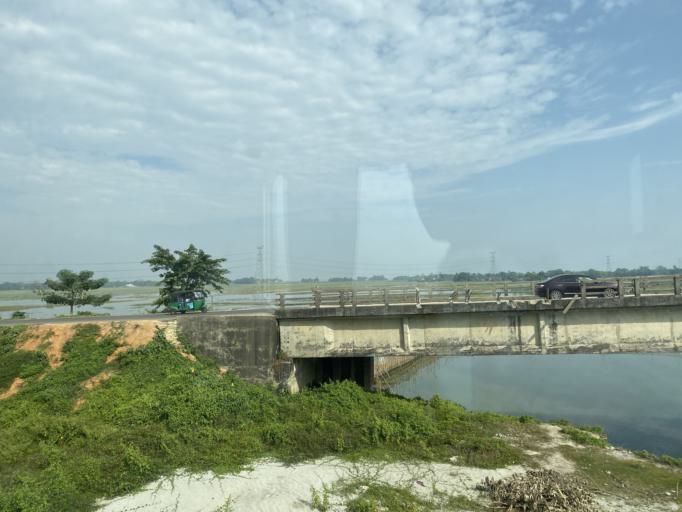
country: IN
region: Tripura
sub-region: West Tripura
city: Agartala
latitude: 23.8796
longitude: 91.1989
